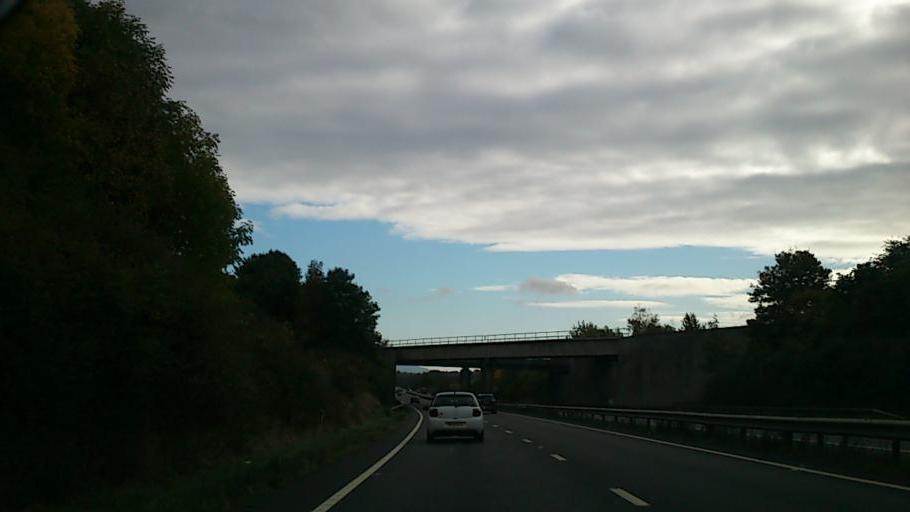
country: GB
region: England
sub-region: Shropshire
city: Bayston Hill
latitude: 52.6835
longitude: -2.7858
